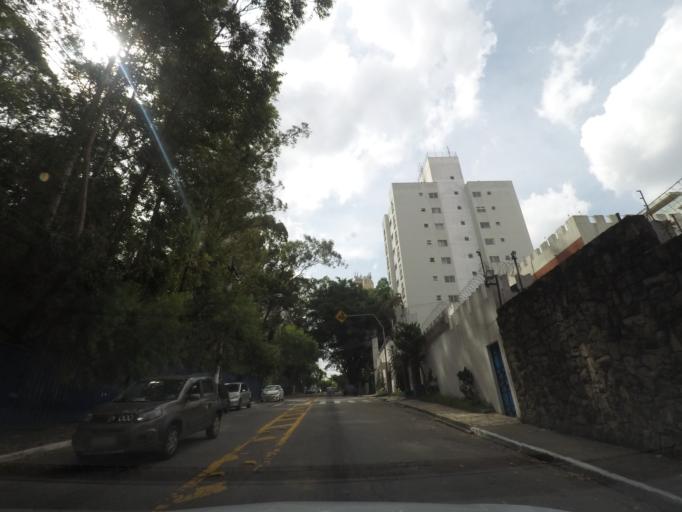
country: BR
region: Sao Paulo
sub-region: Taboao Da Serra
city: Taboao da Serra
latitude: -23.6348
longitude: -46.7378
